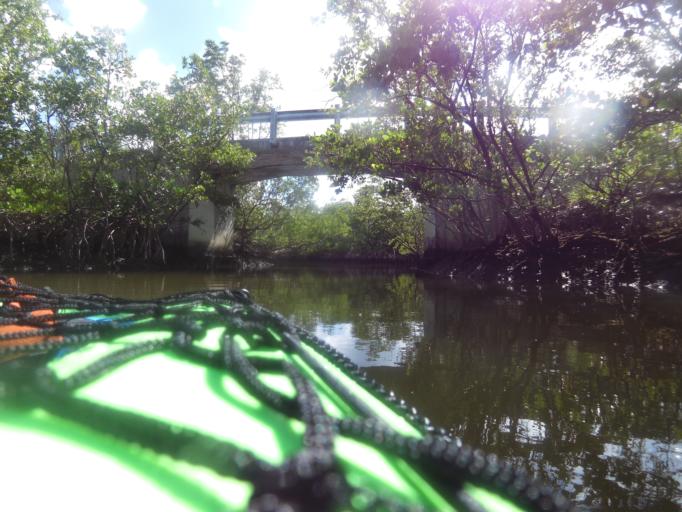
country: US
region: Florida
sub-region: Broward County
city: Hollywood
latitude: 26.0269
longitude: -80.1191
